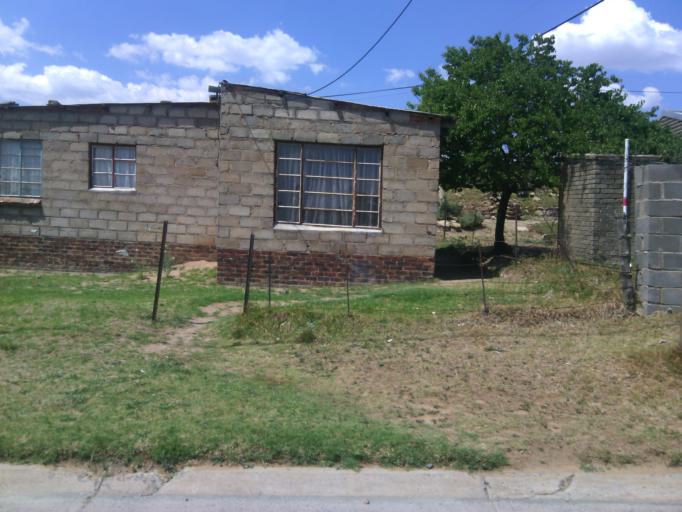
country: ZA
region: Orange Free State
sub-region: Xhariep District Municipality
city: Dewetsdorp
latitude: -29.5852
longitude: 26.6805
